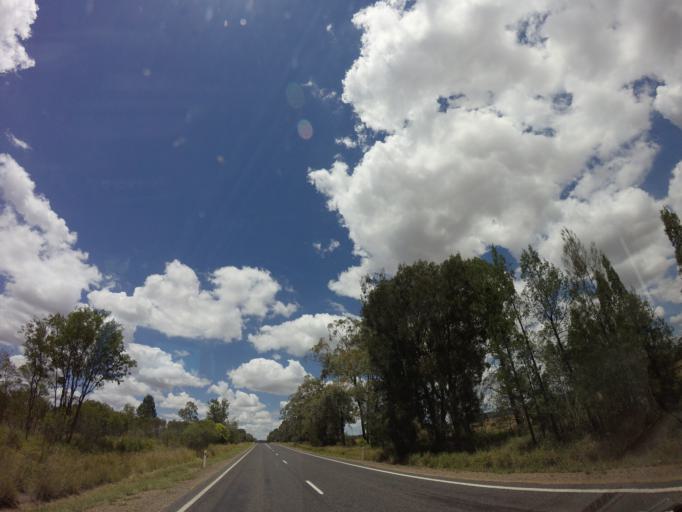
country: AU
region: Queensland
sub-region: Toowoomba
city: Oakey
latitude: -27.9459
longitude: 151.1492
